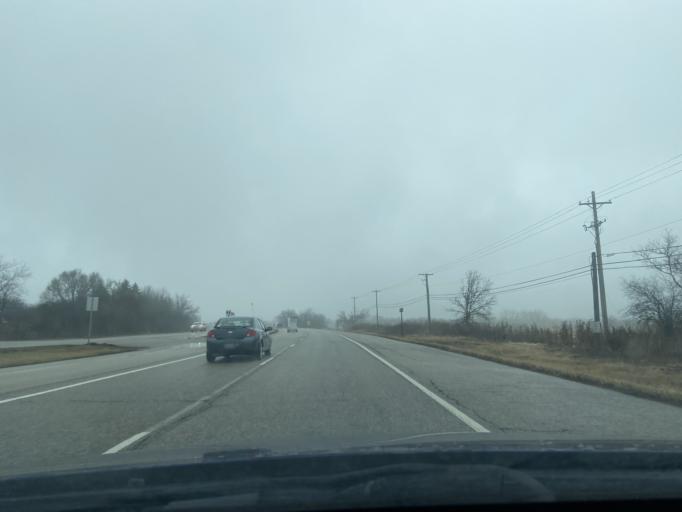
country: US
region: Illinois
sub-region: Lake County
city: Wauconda
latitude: 42.2336
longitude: -88.1114
